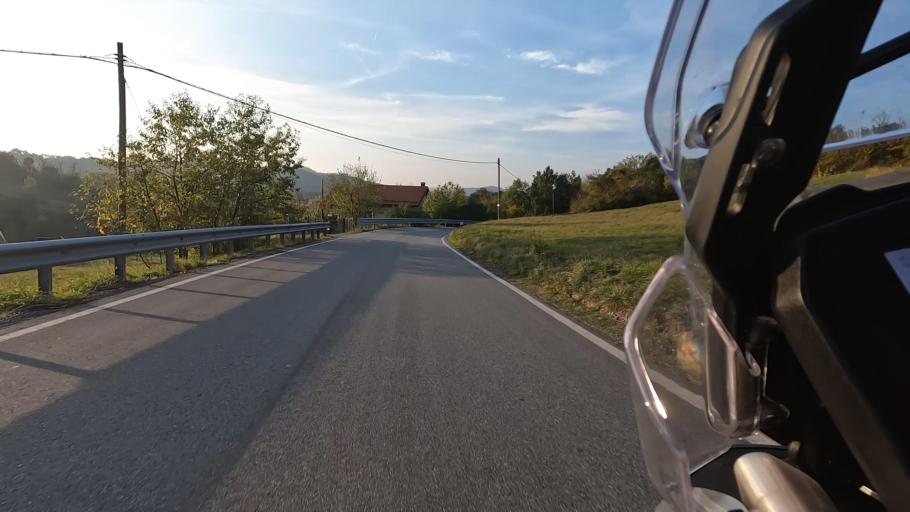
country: IT
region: Liguria
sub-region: Provincia di Savona
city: Sassello
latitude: 44.4896
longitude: 8.4976
